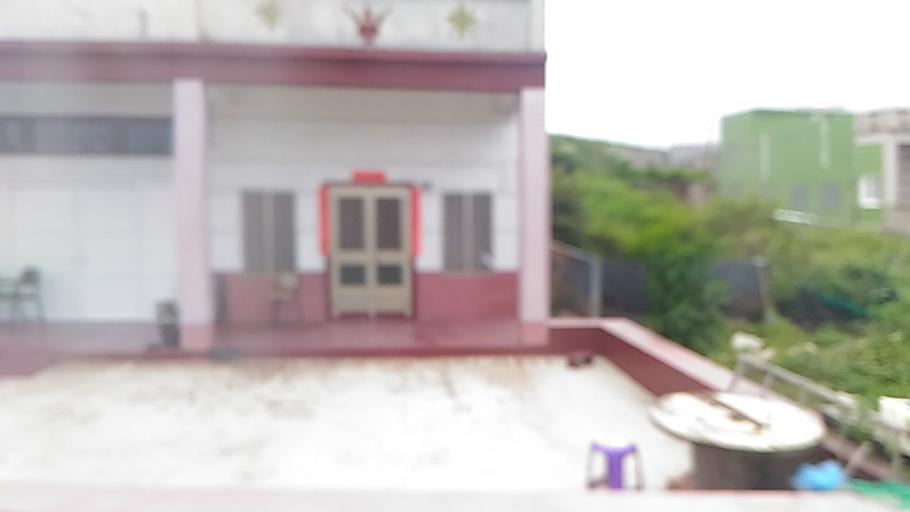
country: TW
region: Taiwan
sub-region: Penghu
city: Ma-kung
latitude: 23.2108
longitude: 119.4370
